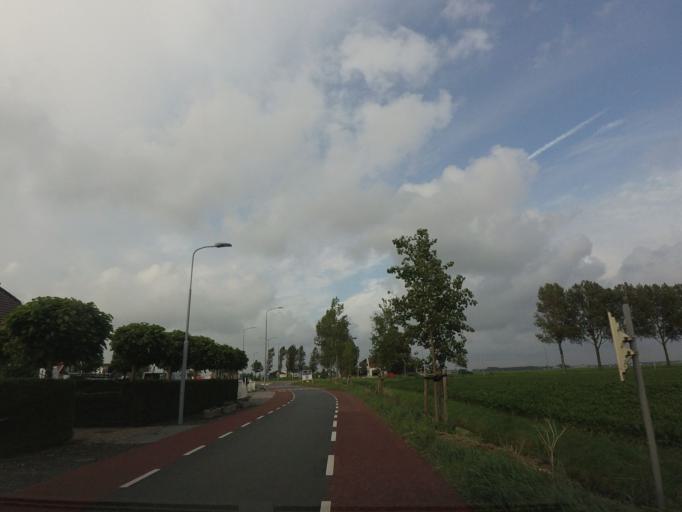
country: NL
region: South Holland
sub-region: Gemeente Kaag en Braassem
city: Leimuiden
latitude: 52.2518
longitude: 4.6557
